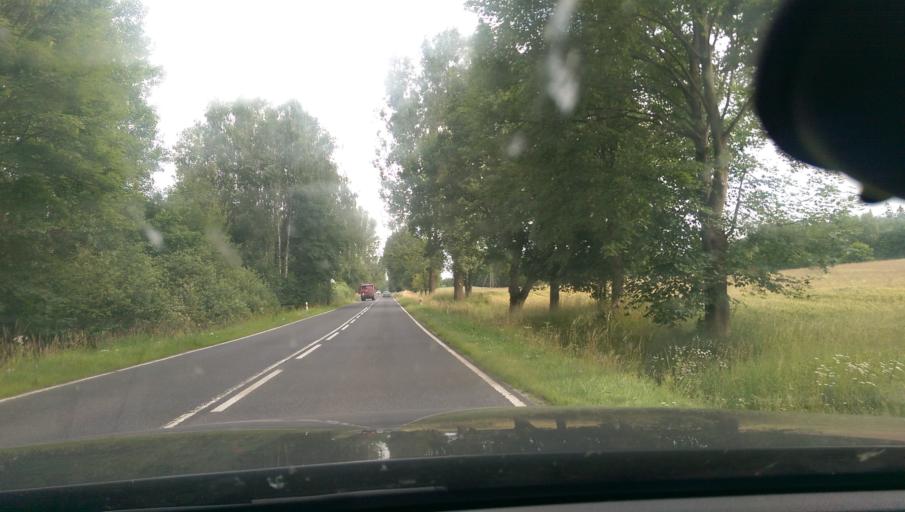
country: PL
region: Warmian-Masurian Voivodeship
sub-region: Powiat wegorzewski
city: Pozezdrze
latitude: 54.1115
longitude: 21.8468
